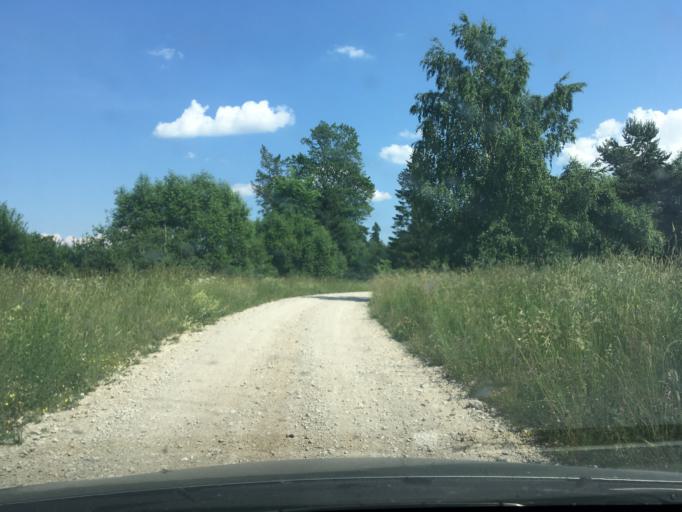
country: EE
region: Raplamaa
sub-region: Maerjamaa vald
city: Marjamaa
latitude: 58.8099
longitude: 24.4398
